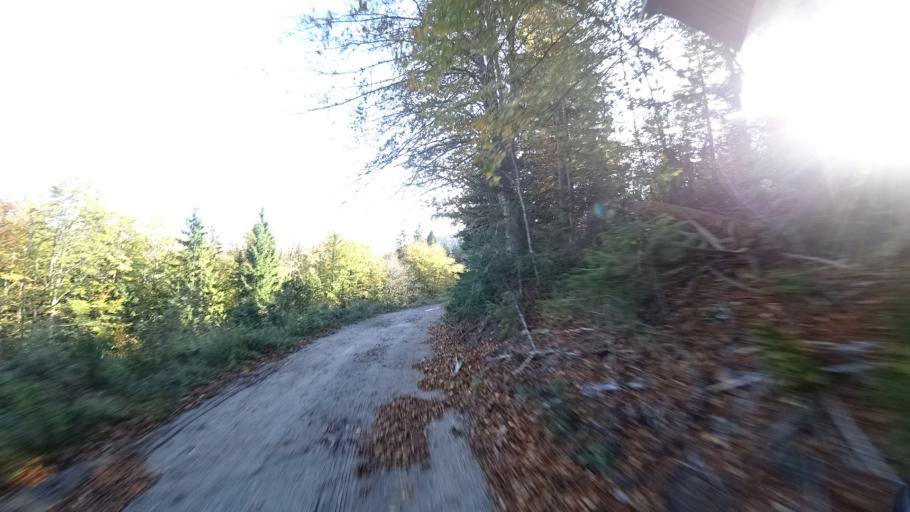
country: HR
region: Karlovacka
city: Plaski
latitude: 44.9485
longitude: 15.4514
